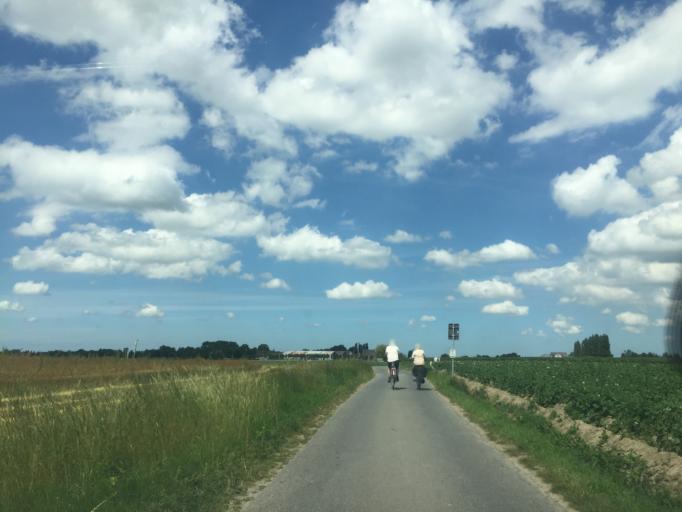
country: BE
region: Flanders
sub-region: Provincie West-Vlaanderen
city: Staden
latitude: 50.9988
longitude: 3.0197
